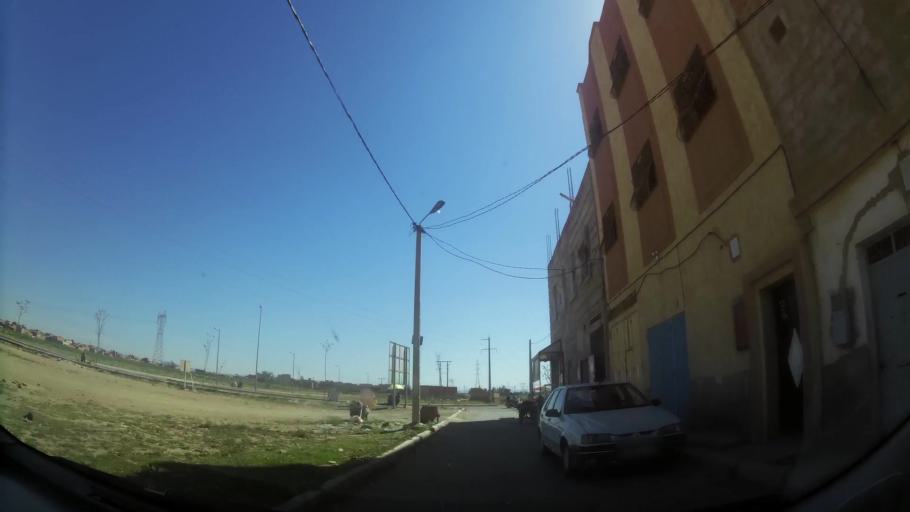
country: MA
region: Oriental
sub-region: Oujda-Angad
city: Oujda
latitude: 34.7209
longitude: -1.9042
